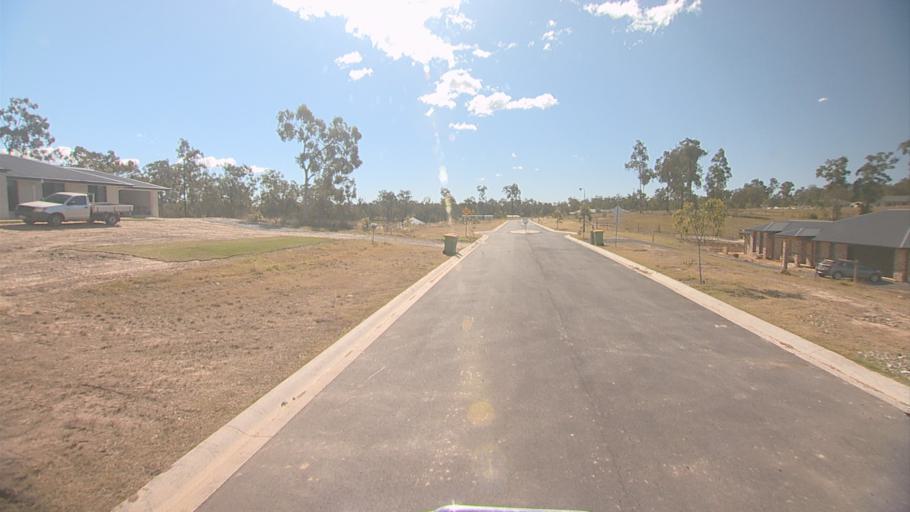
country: AU
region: Queensland
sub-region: Logan
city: North Maclean
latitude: -27.7617
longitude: 152.9311
